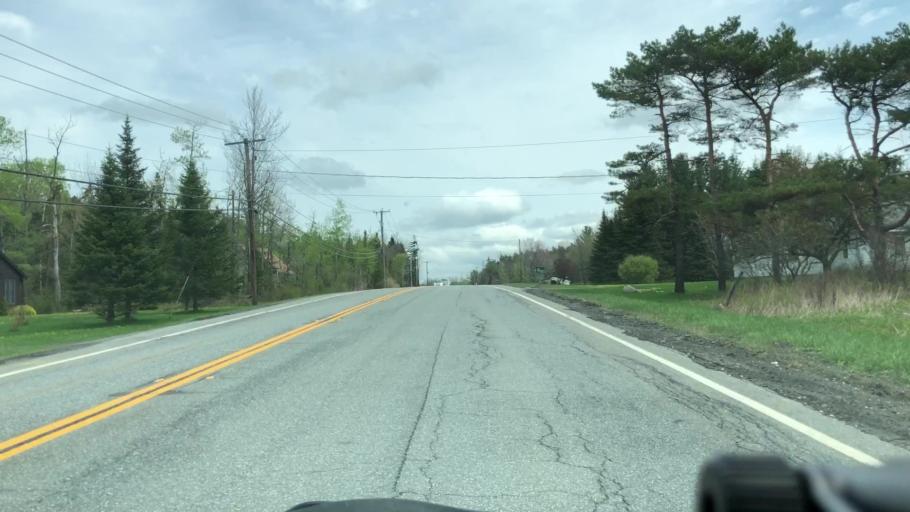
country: US
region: Massachusetts
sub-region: Berkshire County
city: Hinsdale
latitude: 42.5060
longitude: -73.0930
